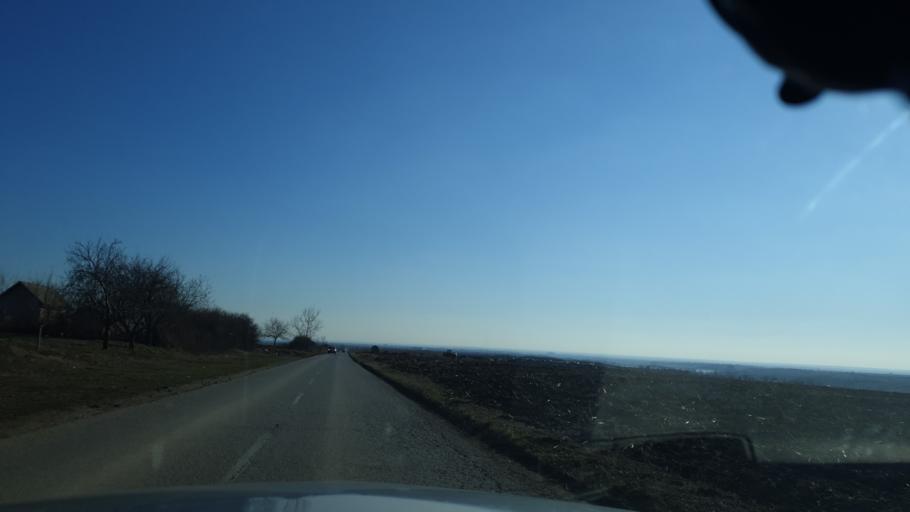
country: RS
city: Vrdnik
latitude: 45.0908
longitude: 19.8060
